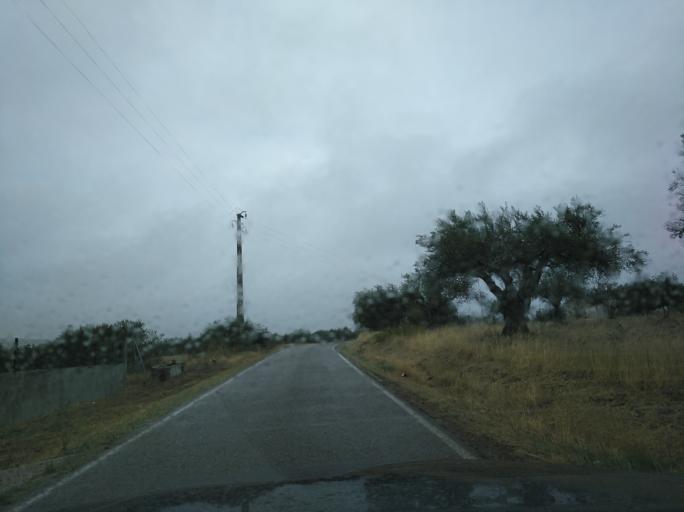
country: PT
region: Portalegre
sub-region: Campo Maior
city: Campo Maior
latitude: 38.9515
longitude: -7.0859
